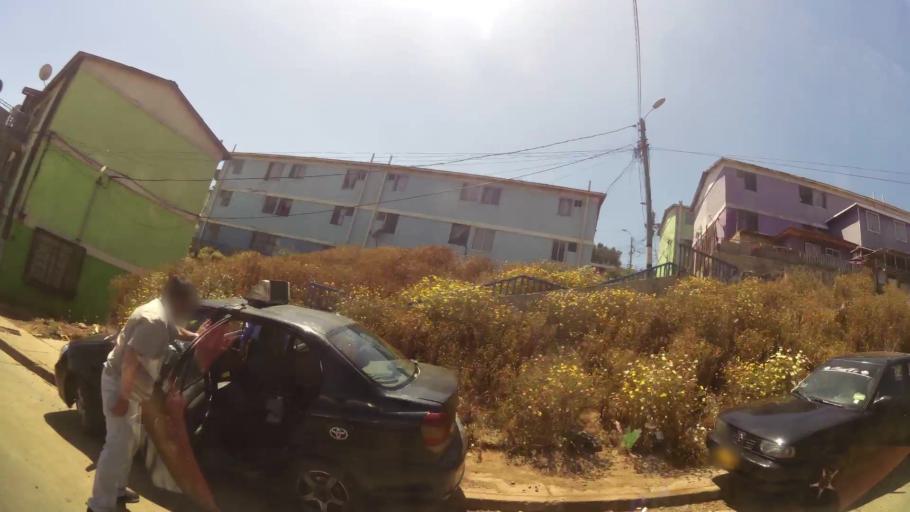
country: CL
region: Valparaiso
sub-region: Provincia de Valparaiso
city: Valparaiso
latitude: -33.0348
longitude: -71.6547
